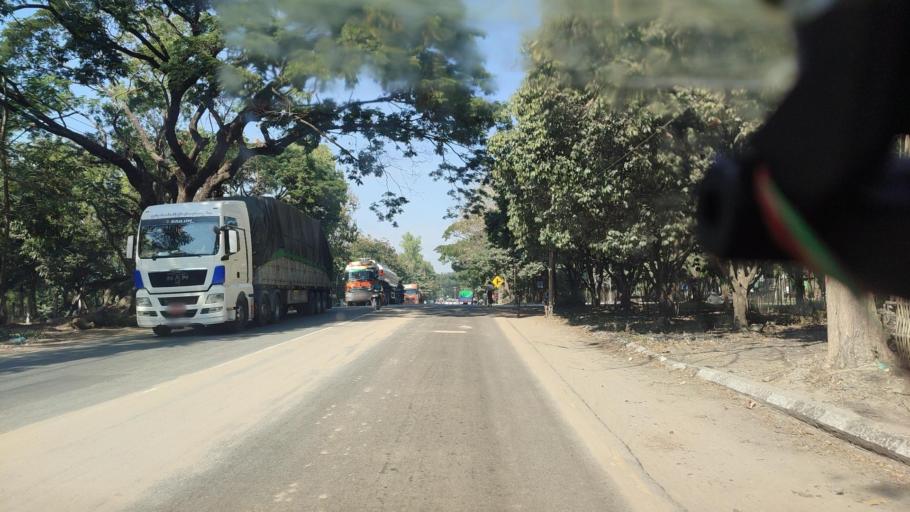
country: MM
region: Mandalay
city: Pyinmana
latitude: 19.4844
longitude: 96.2651
